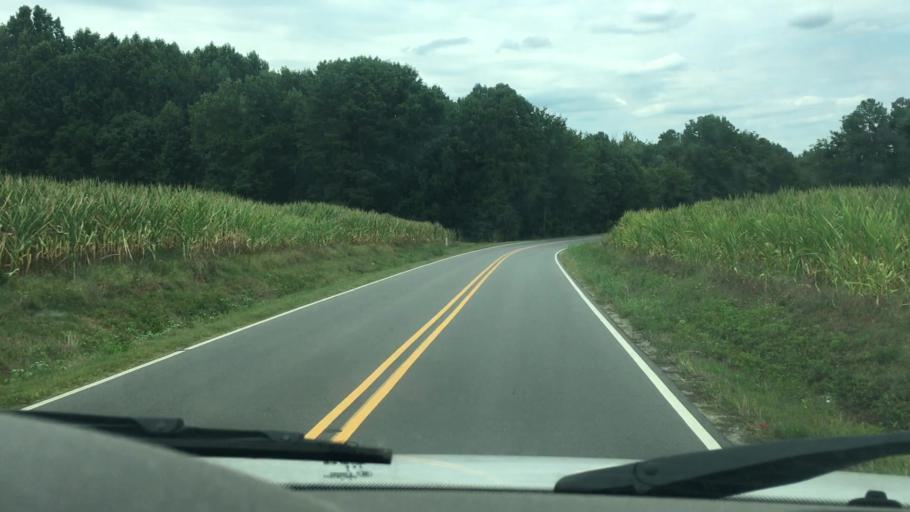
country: US
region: North Carolina
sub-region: Gaston County
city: Davidson
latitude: 35.4564
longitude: -80.8016
